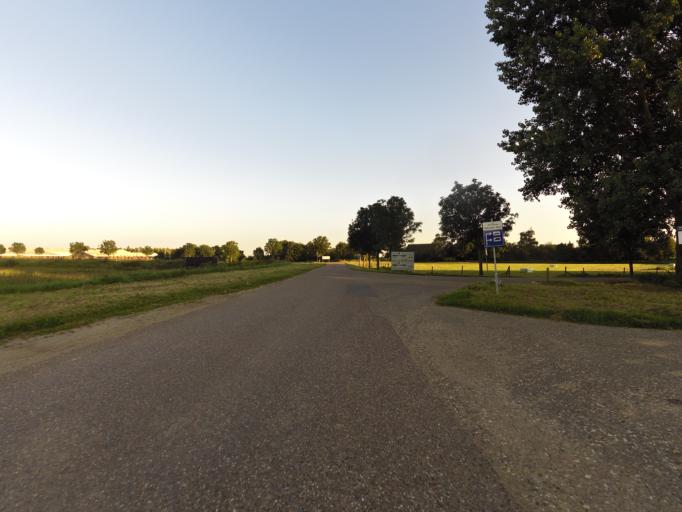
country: NL
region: Gelderland
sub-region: Gemeente Zevenaar
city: Zevenaar
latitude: 51.8760
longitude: 6.0504
